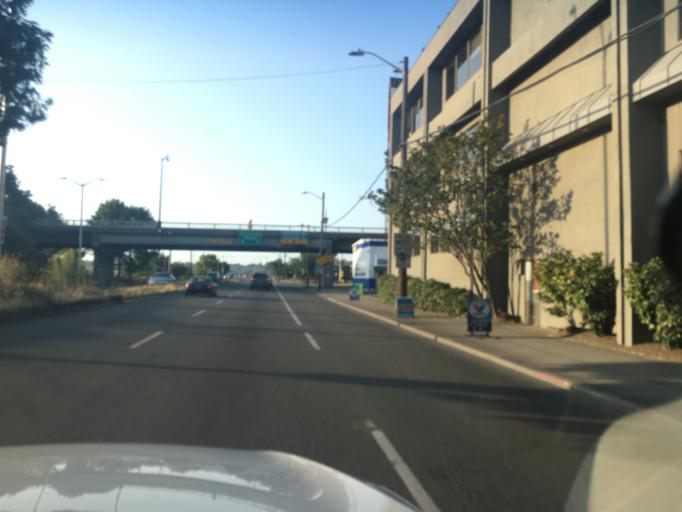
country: US
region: Washington
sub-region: King County
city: Seattle
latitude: 47.6523
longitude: -122.3762
